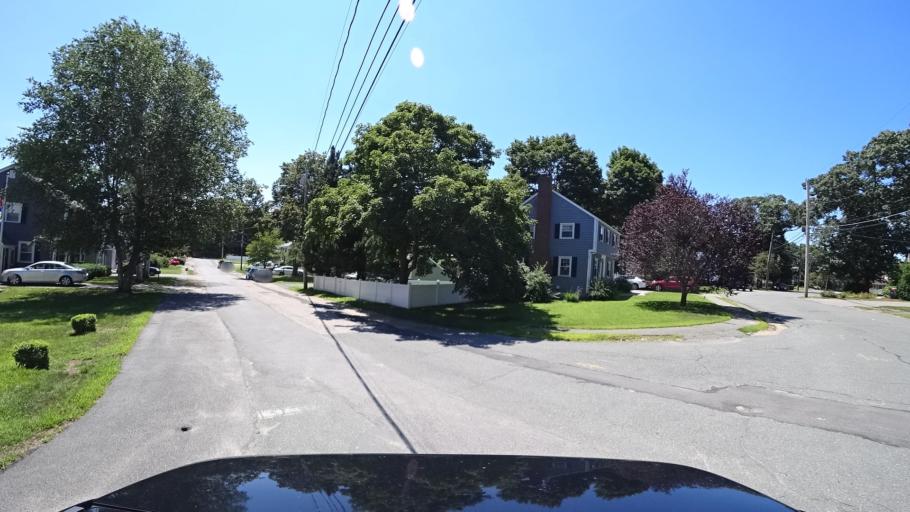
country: US
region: Massachusetts
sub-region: Norfolk County
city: Dedham
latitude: 42.2359
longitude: -71.1559
